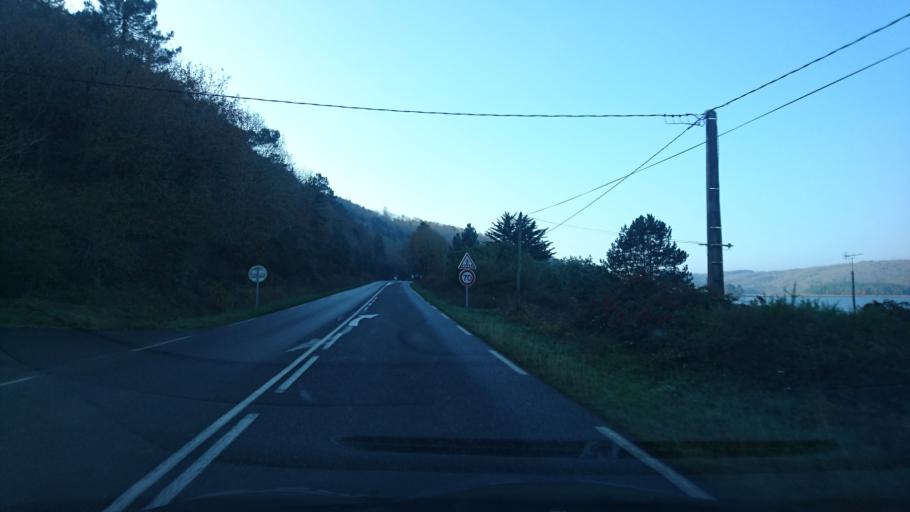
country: FR
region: Brittany
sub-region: Departement du Finistere
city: Hopital-Camfrout
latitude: 48.2807
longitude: -4.2577
